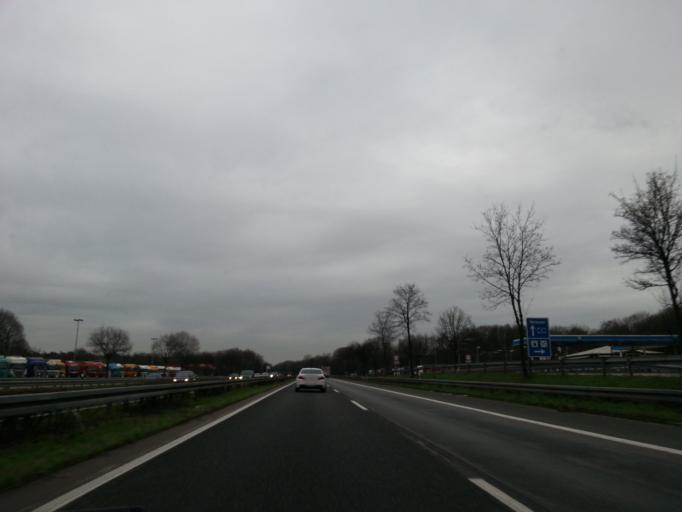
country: DE
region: North Rhine-Westphalia
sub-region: Regierungsbezirk Dusseldorf
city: Hunxe
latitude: 51.6375
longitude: 6.7450
